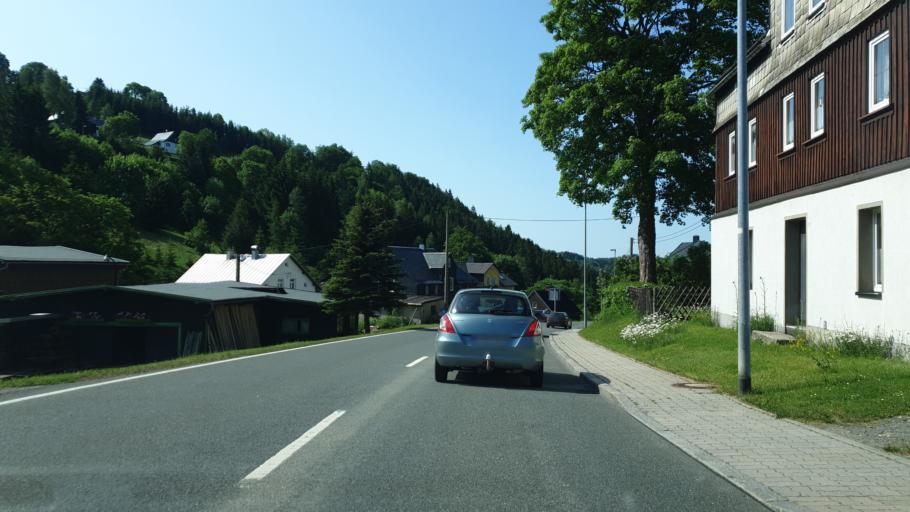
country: DE
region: Saxony
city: Klingenthal
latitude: 50.3915
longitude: 12.4949
